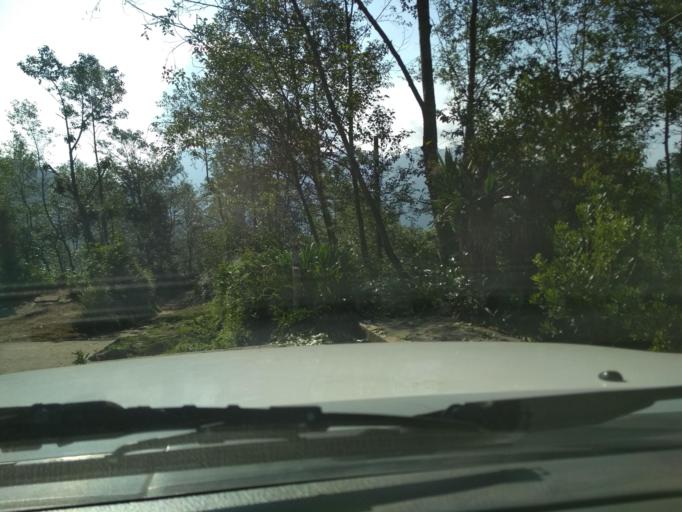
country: MX
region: Veracruz
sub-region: La Perla
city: Chilapa
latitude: 18.9846
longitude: -97.1622
